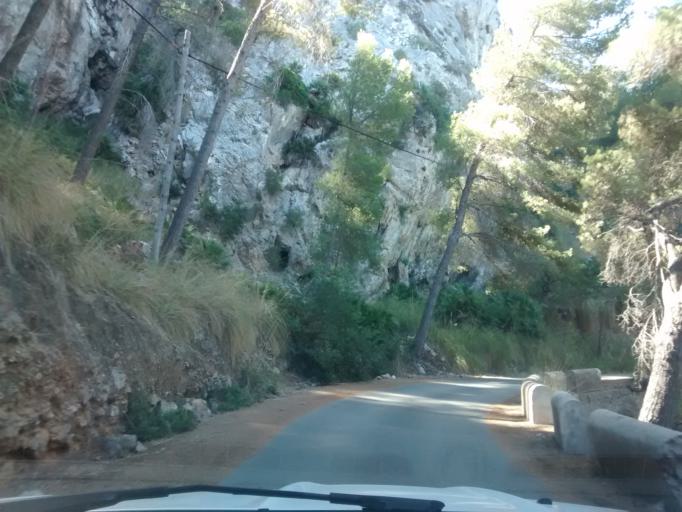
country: ES
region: Balearic Islands
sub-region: Illes Balears
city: Port d'Alcudia
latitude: 39.8798
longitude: 3.1772
